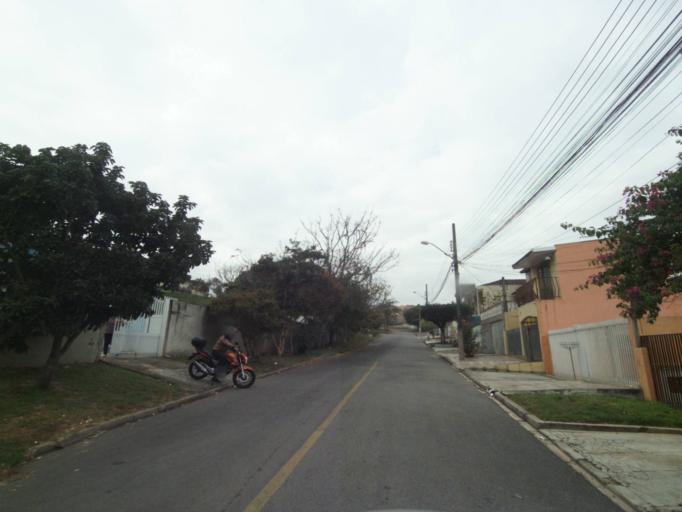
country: BR
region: Parana
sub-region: Curitiba
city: Curitiba
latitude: -25.5132
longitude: -49.3244
